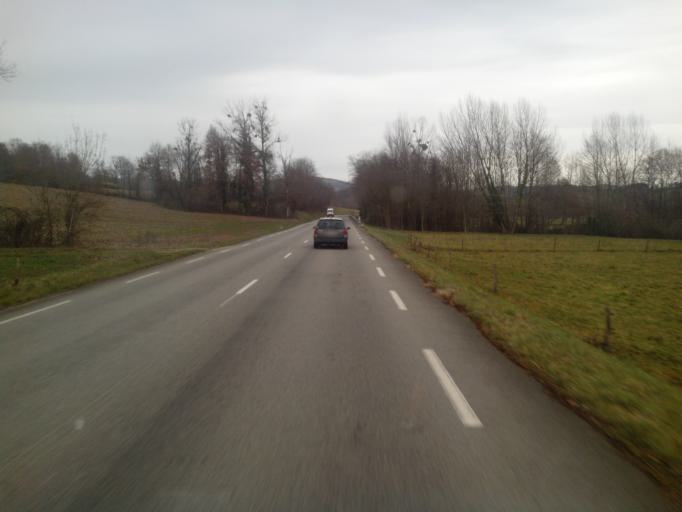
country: FR
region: Midi-Pyrenees
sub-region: Departement de l'Ariege
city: Montjoie-en-Couserans
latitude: 43.0038
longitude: 1.3543
